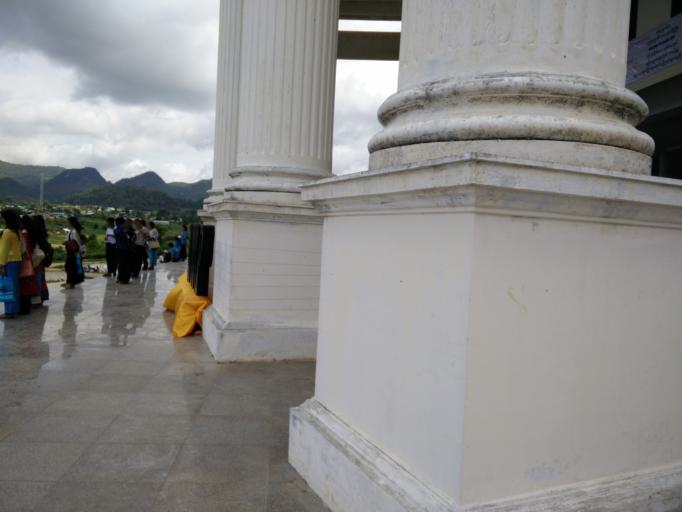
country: MM
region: Shan
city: Lashio
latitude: 23.0311
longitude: 97.7733
